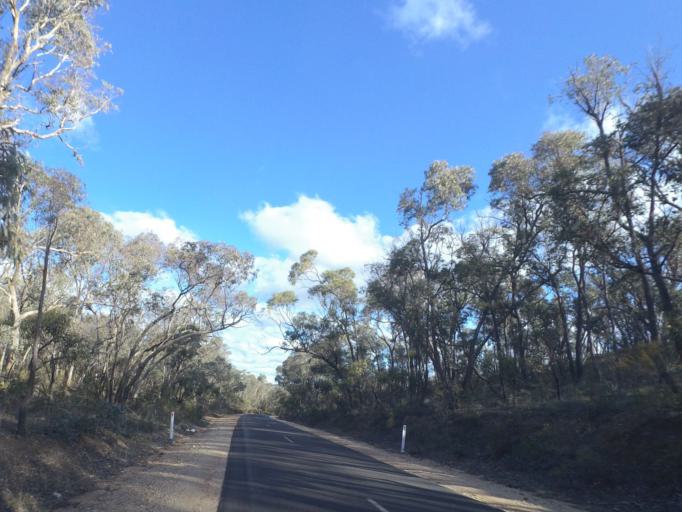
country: AU
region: Victoria
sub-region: Mount Alexander
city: Castlemaine
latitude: -37.1535
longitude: 144.2322
